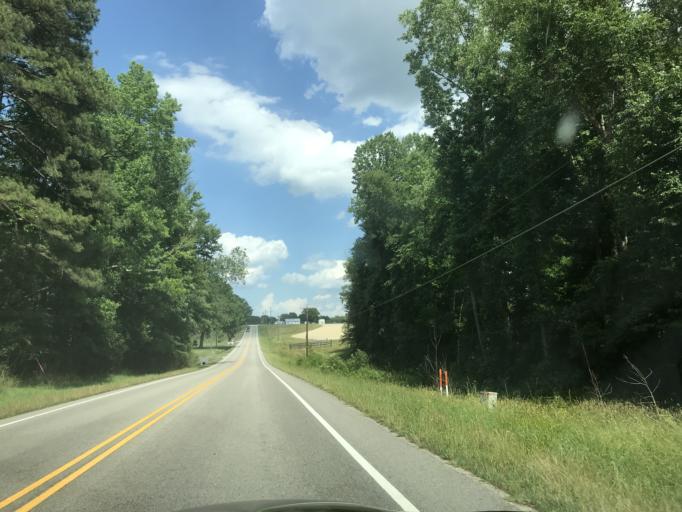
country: US
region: North Carolina
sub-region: Wake County
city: Zebulon
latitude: 35.9589
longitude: -78.2657
